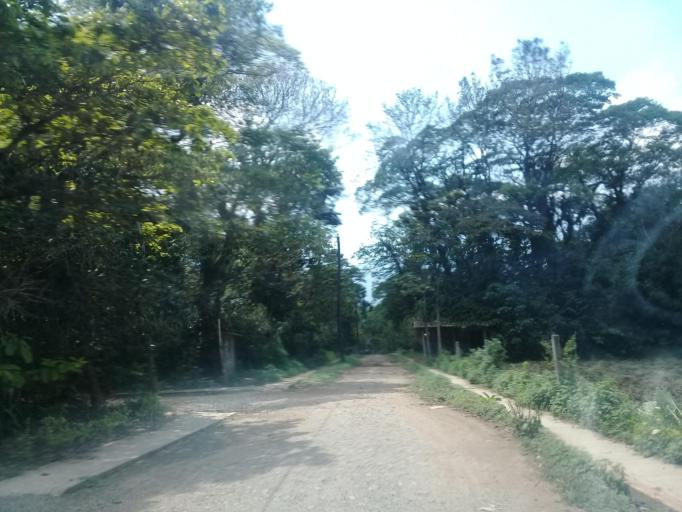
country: MX
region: Veracruz
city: Jalapilla
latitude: 18.8195
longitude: -97.0630
